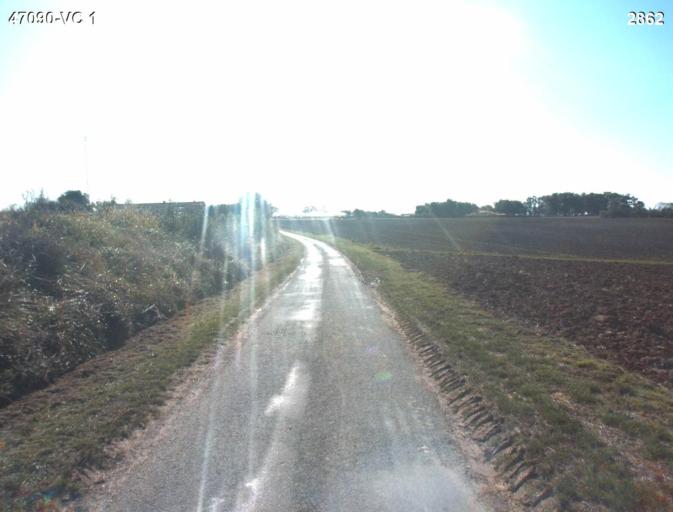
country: FR
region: Aquitaine
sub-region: Departement du Lot-et-Garonne
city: Nerac
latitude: 44.1535
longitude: 0.3966
